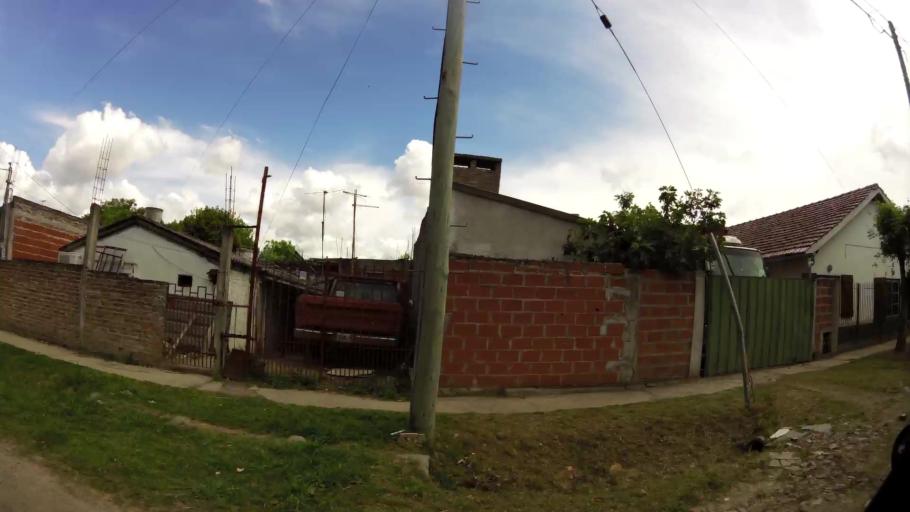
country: AR
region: Buenos Aires
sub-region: Partido de Quilmes
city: Quilmes
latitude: -34.7796
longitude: -58.2751
